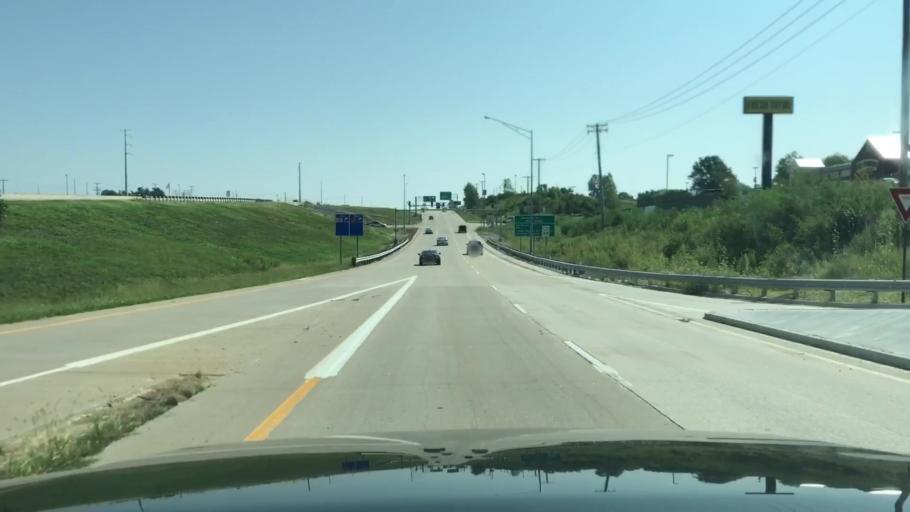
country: US
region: Missouri
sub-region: Saint Charles County
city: Saint Peters
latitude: 38.7473
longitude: -90.5865
